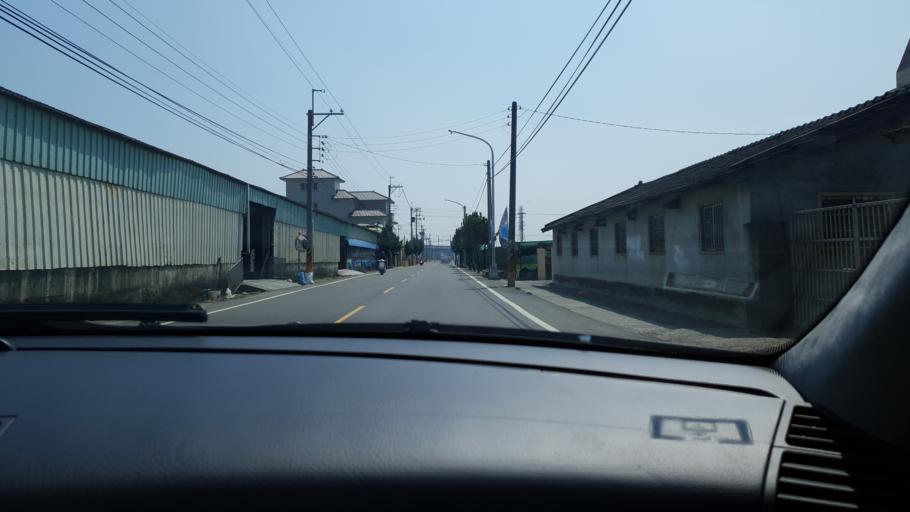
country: TW
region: Taiwan
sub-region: Yunlin
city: Douliu
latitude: 23.7558
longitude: 120.4209
